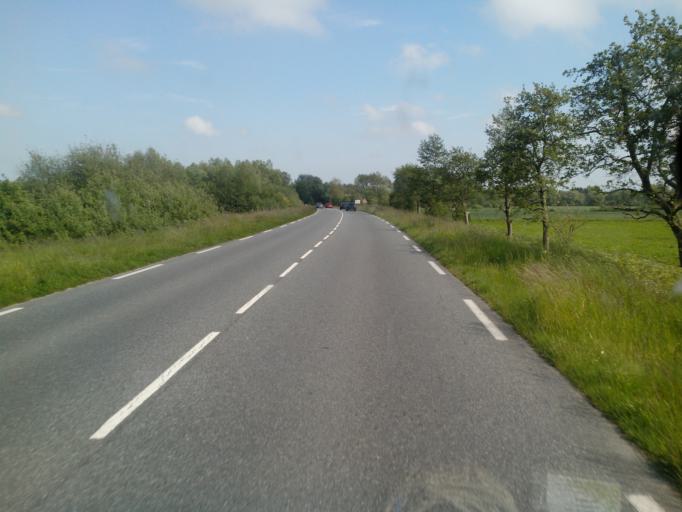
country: FR
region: Picardie
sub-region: Departement de la Somme
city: Rue
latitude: 50.2647
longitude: 1.6576
